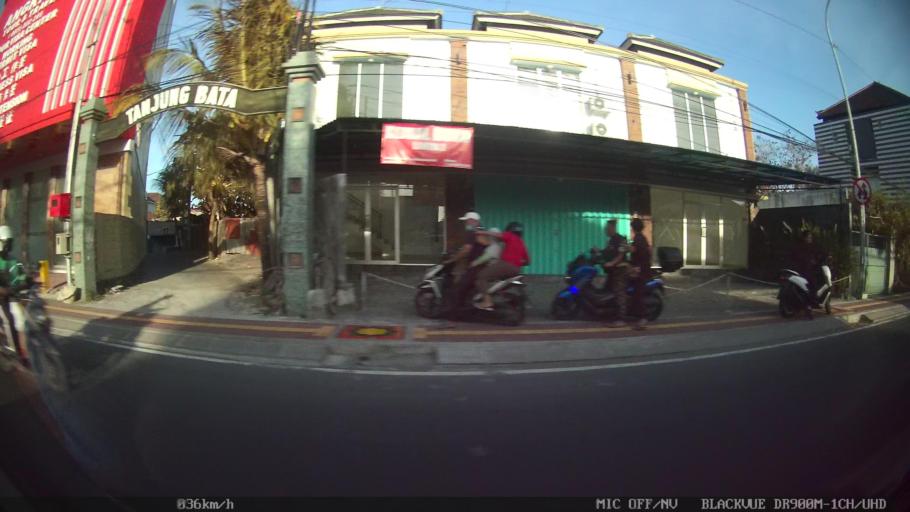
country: ID
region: Bali
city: Jimbaran
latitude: -8.7857
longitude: 115.1705
